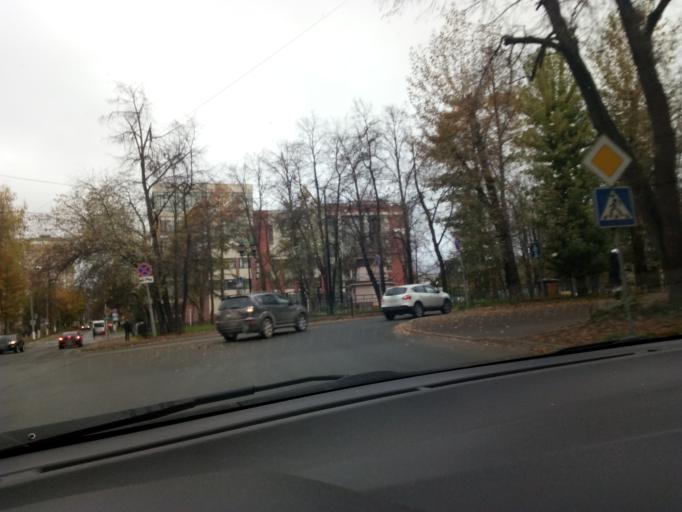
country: RU
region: Tatarstan
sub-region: Gorod Kazan'
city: Kazan
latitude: 55.7871
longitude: 49.1478
